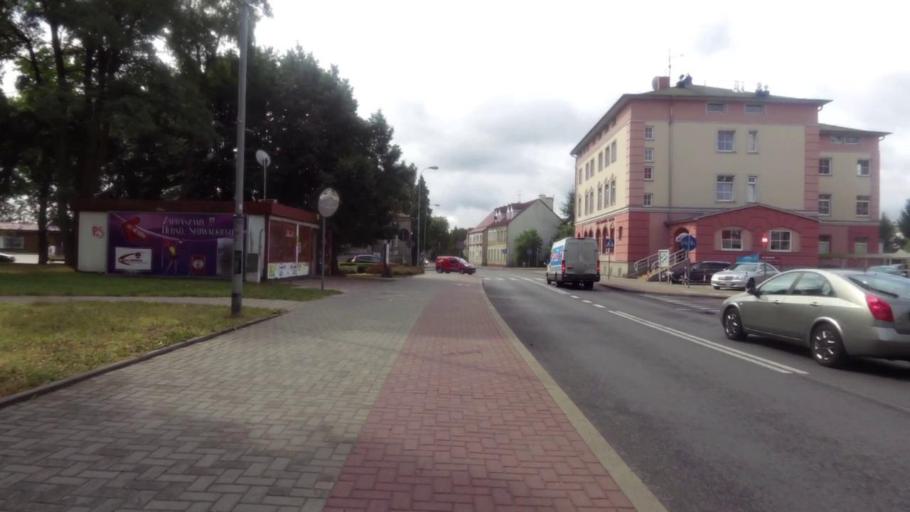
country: PL
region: West Pomeranian Voivodeship
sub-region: Powiat mysliborski
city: Debno
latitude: 52.7355
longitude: 14.6958
